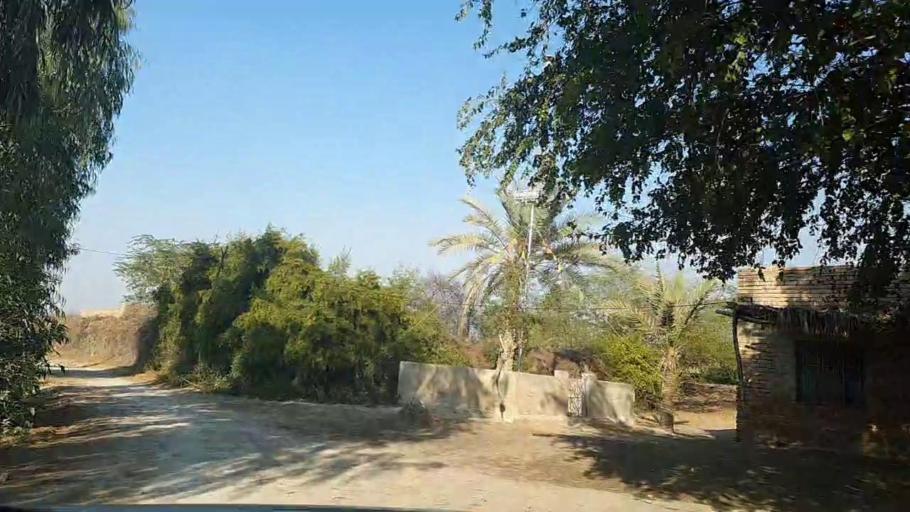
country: PK
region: Sindh
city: Daur
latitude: 26.3268
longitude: 68.1773
